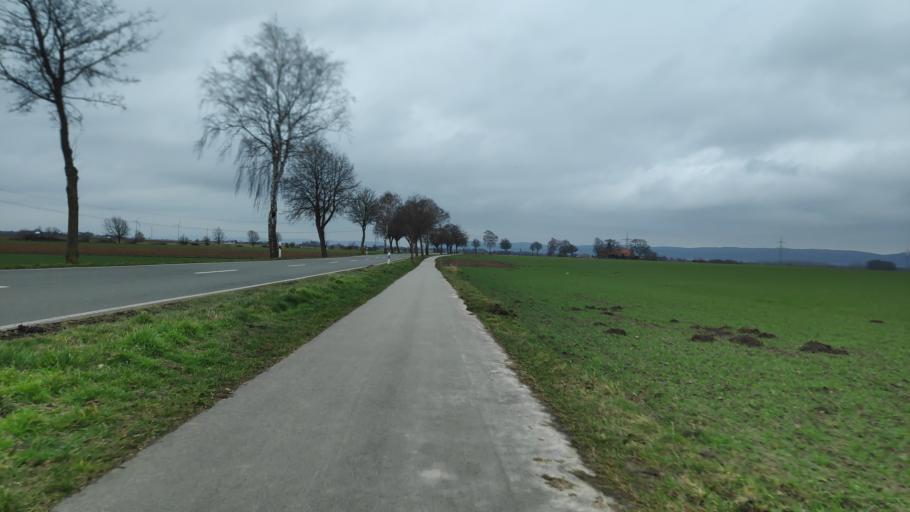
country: DE
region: North Rhine-Westphalia
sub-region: Regierungsbezirk Detmold
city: Hille
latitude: 52.3326
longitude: 8.8061
